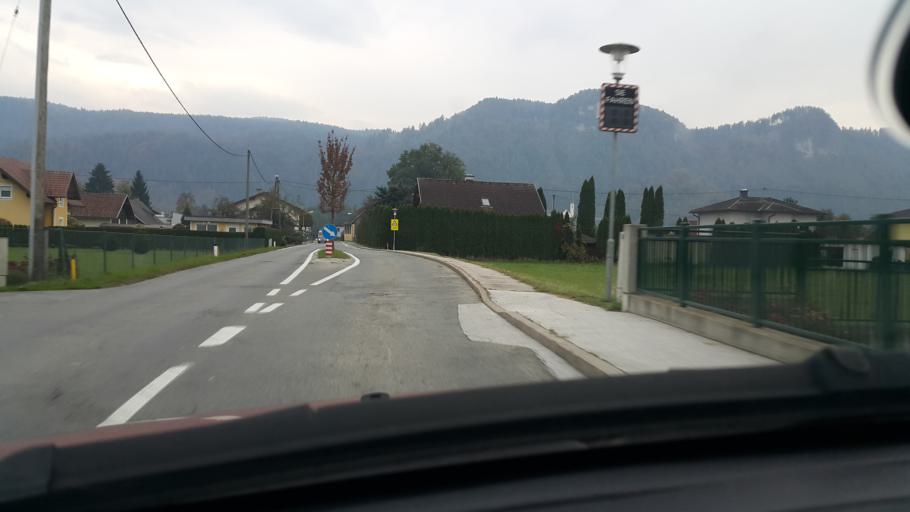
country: AT
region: Carinthia
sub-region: Politischer Bezirk Klagenfurt Land
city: Ebenthal
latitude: 46.6122
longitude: 14.3980
